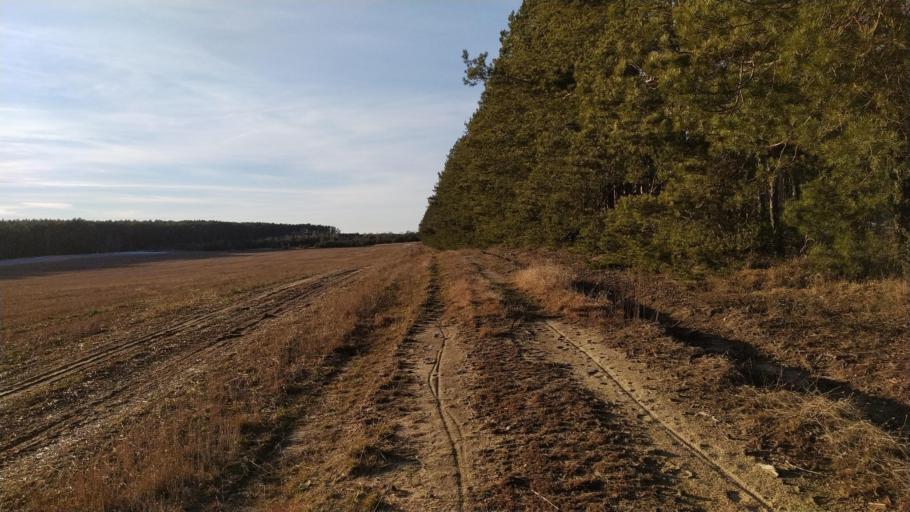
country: BY
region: Brest
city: Kamyanyets
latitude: 52.3703
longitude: 23.8553
